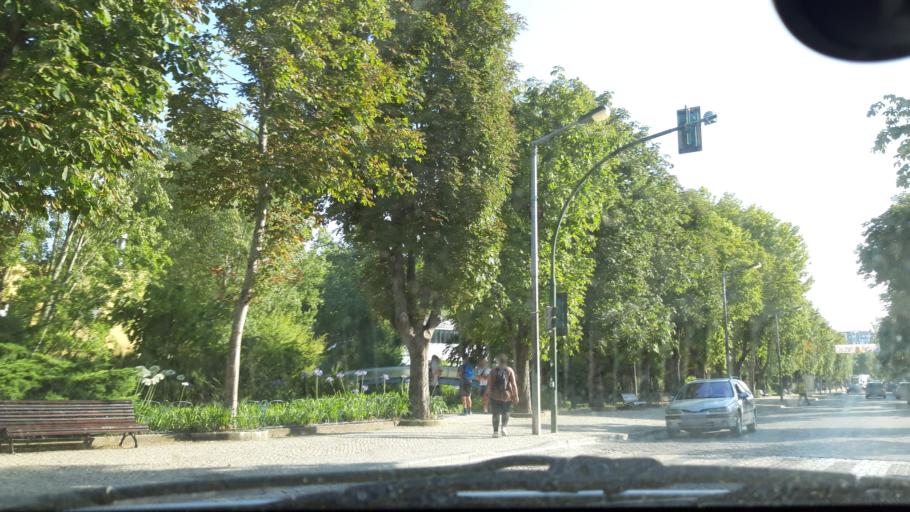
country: PT
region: Santarem
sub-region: Torres Novas
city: Torres Novas
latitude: 39.4821
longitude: -8.5392
